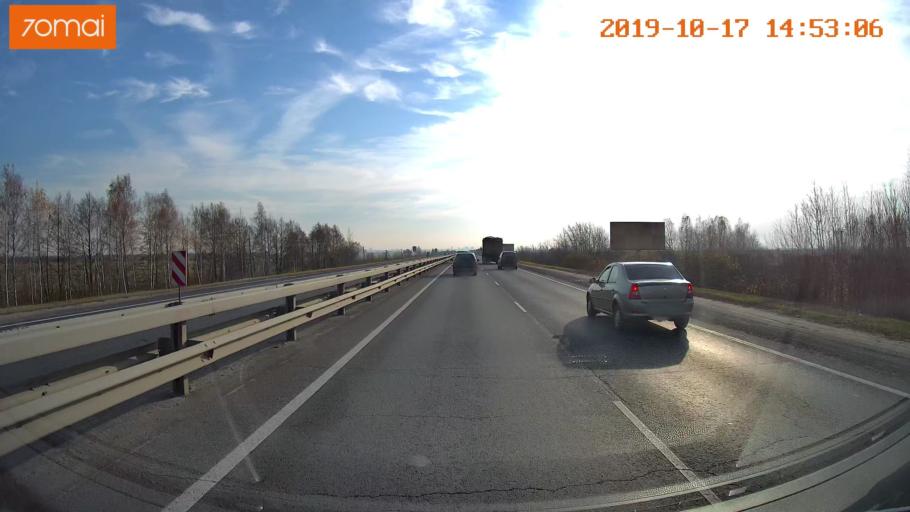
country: RU
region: Rjazan
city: Polyany
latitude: 54.6984
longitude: 39.8408
